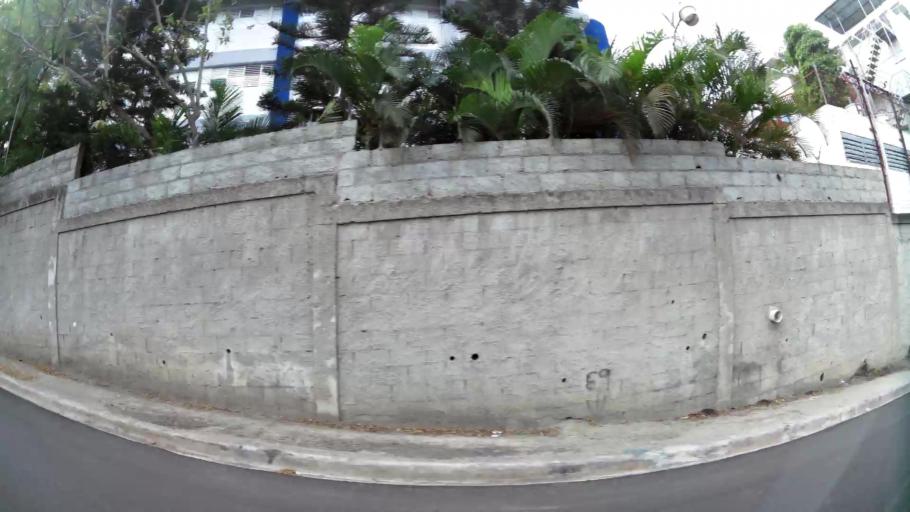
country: DO
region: Santiago
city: Santiago de los Caballeros
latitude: 19.4268
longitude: -70.6726
